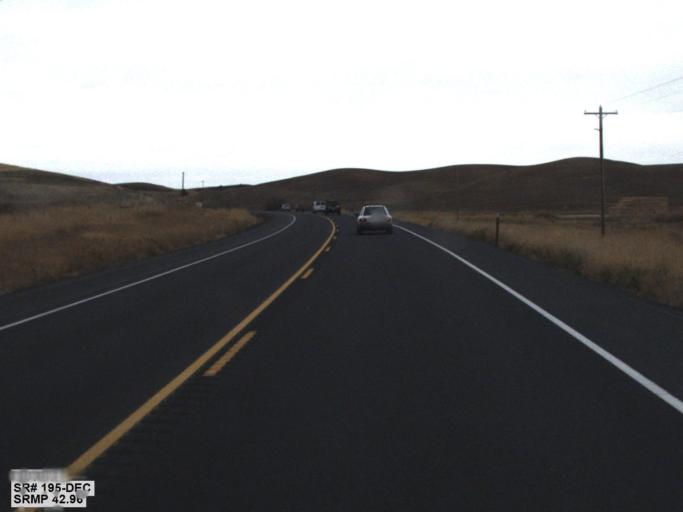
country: US
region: Washington
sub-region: Whitman County
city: Colfax
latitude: 46.9450
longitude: -117.3354
